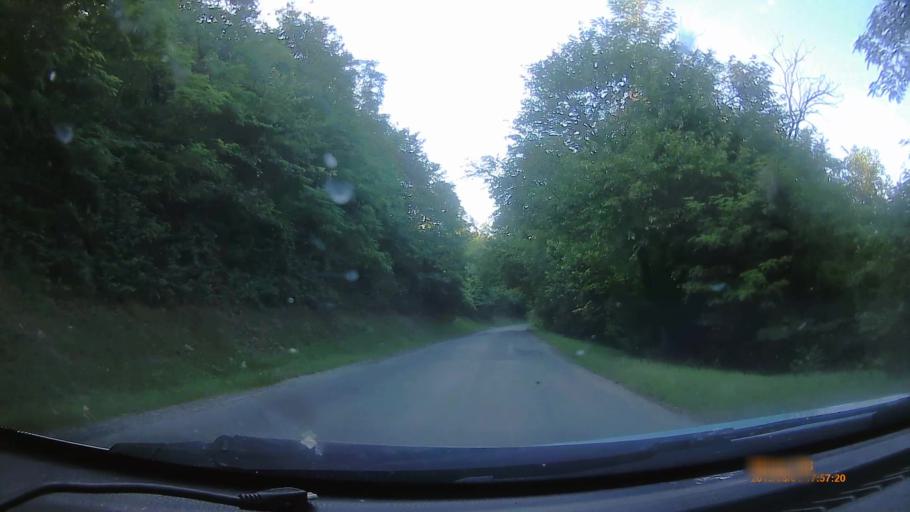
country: HU
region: Baranya
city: Sasd
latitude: 46.2000
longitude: 18.1146
